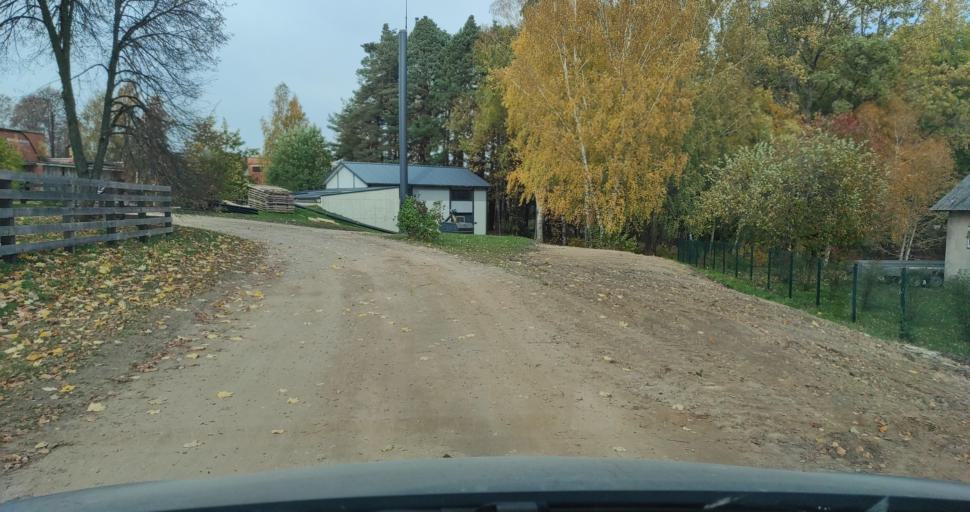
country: LV
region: Kuldigas Rajons
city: Kuldiga
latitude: 56.9623
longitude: 21.9220
